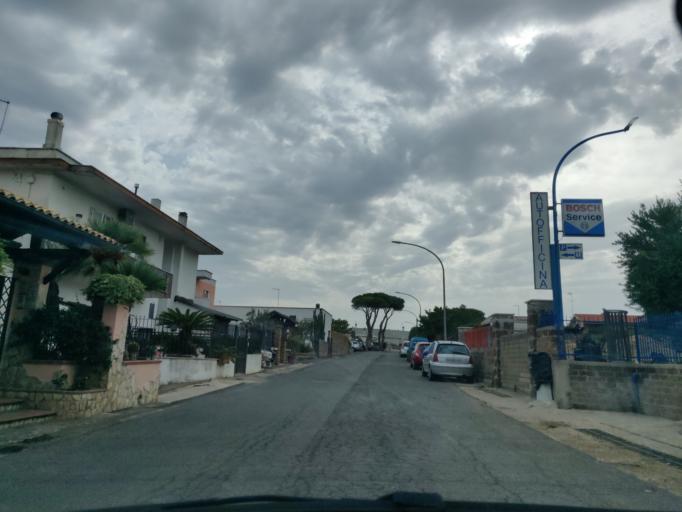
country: IT
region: Latium
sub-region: Citta metropolitana di Roma Capitale
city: Santa Marinella
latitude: 42.0416
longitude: 11.9025
